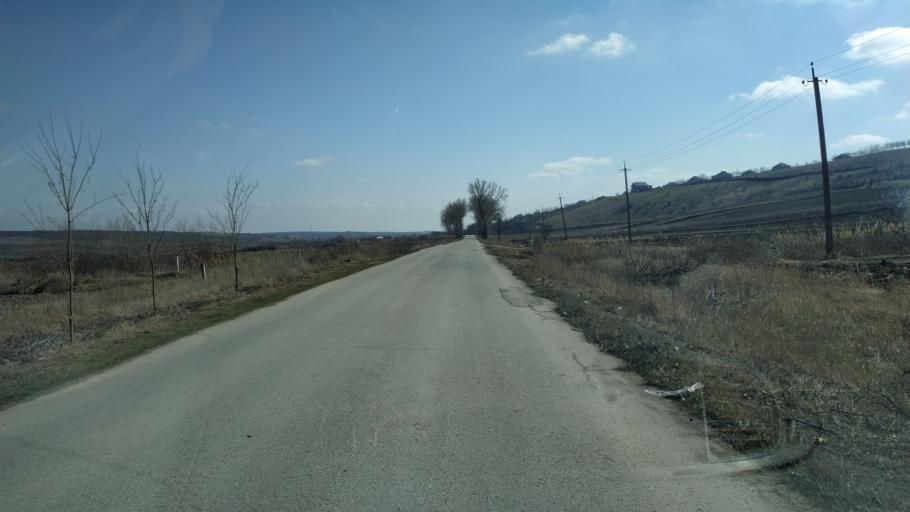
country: MD
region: Hincesti
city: Hincesti
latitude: 46.9410
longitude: 28.6274
